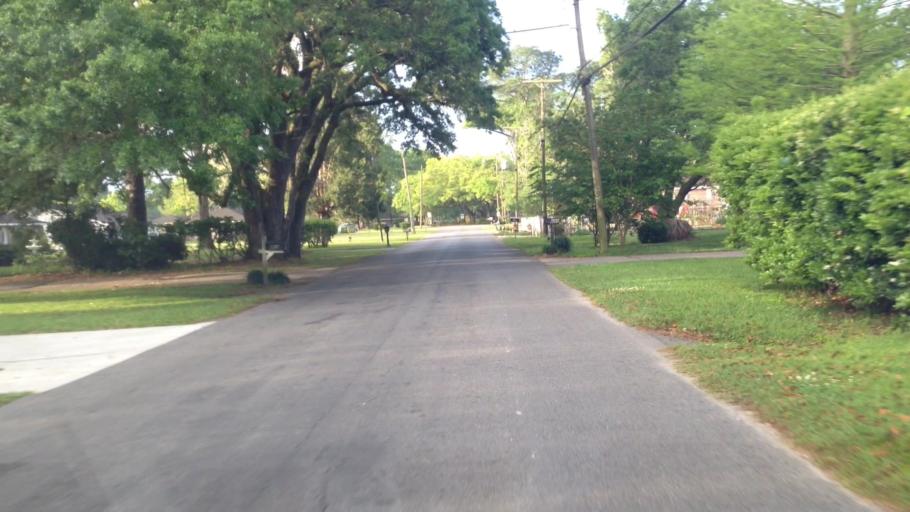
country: US
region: Louisiana
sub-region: Jefferson Parish
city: Jefferson
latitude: 29.9462
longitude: -90.1525
